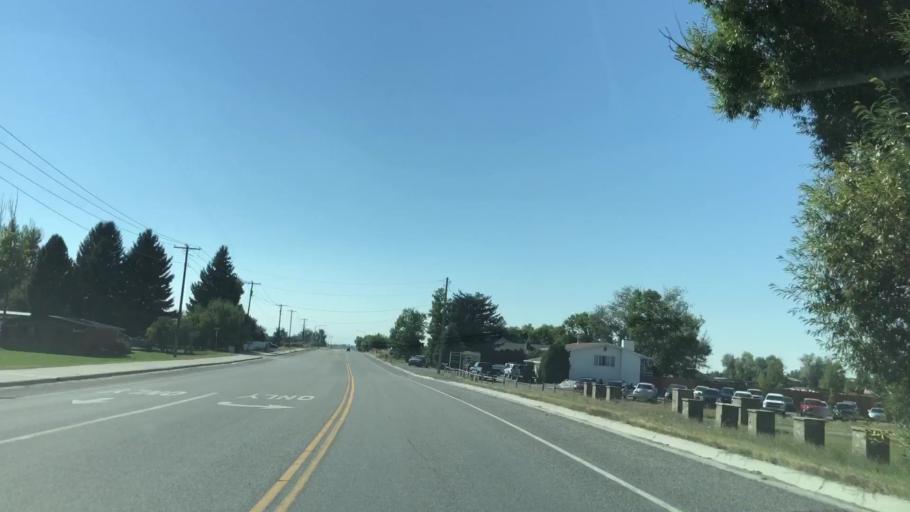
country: US
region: Montana
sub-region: Gallatin County
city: Bozeman
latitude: 45.7293
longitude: -111.0927
